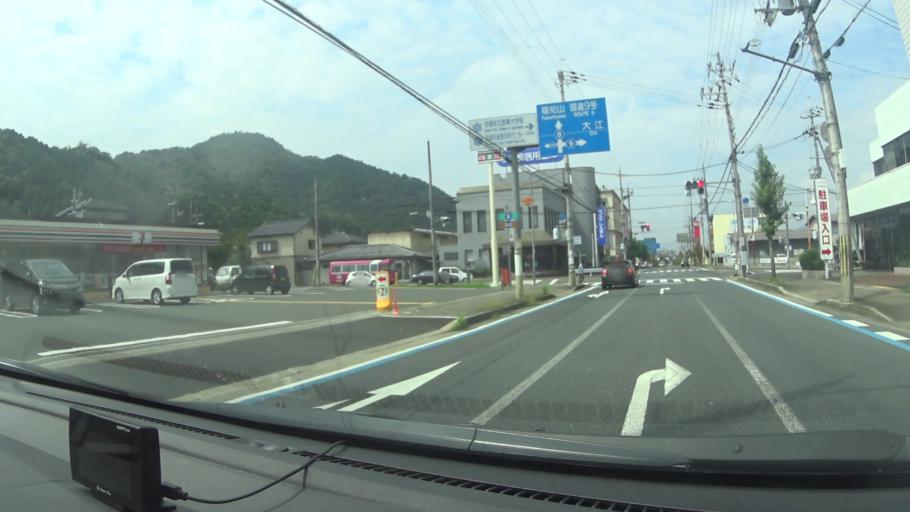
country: JP
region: Kyoto
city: Ayabe
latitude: 35.2998
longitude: 135.2600
